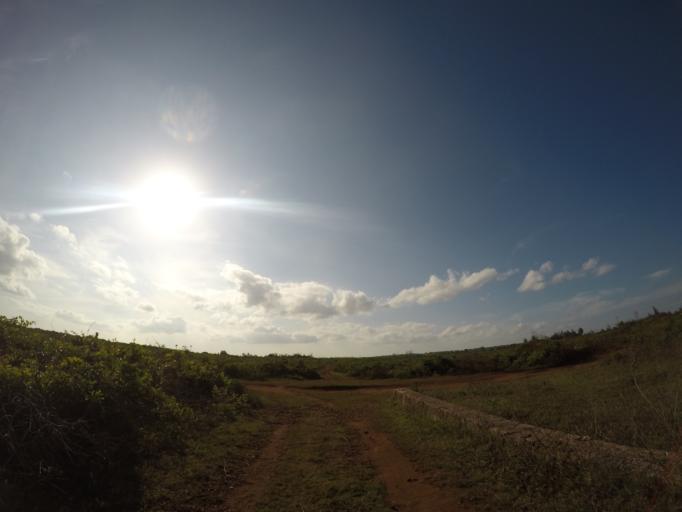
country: TZ
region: Zanzibar Central/South
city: Koani
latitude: -6.2061
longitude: 39.3148
